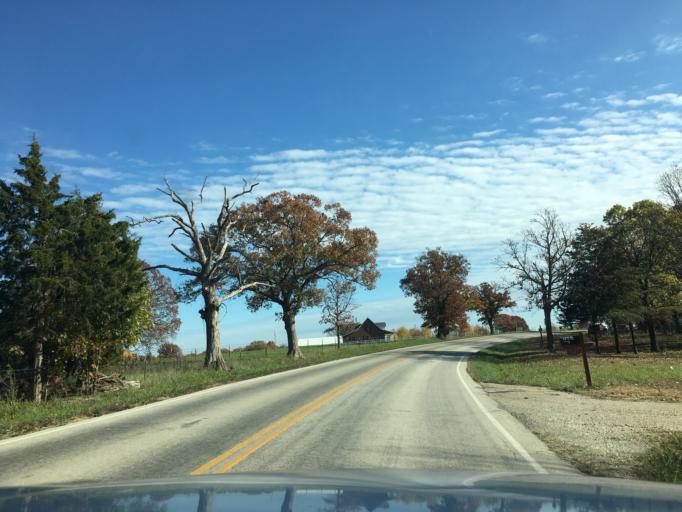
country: US
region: Missouri
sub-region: Maries County
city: Belle
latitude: 38.3038
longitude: -91.7281
